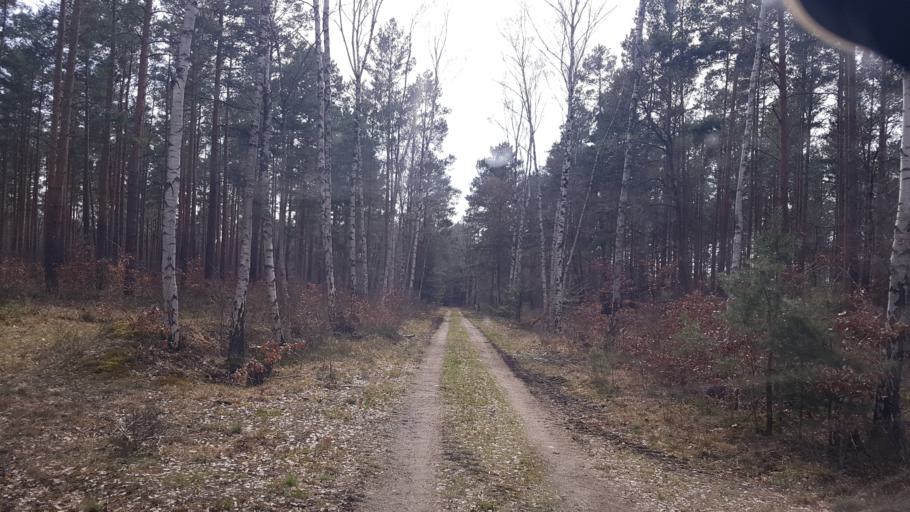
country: DE
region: Brandenburg
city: Lauchhammer
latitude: 51.5381
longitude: 13.7078
